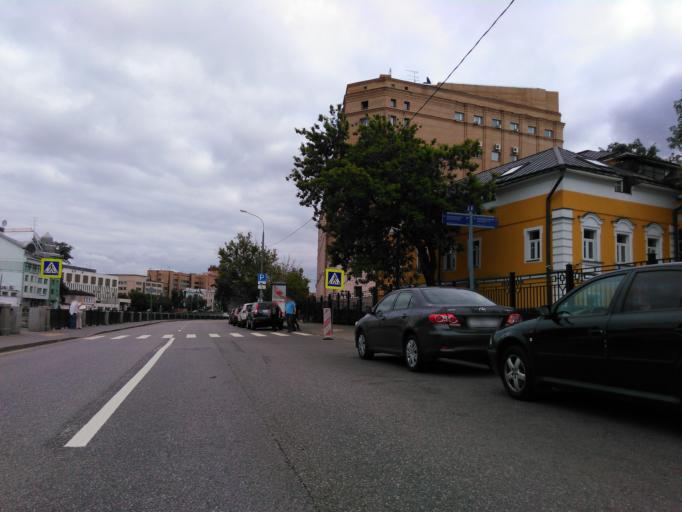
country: RU
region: Moscow
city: Zamoskvorech'ye
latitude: 55.7457
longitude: 37.6300
